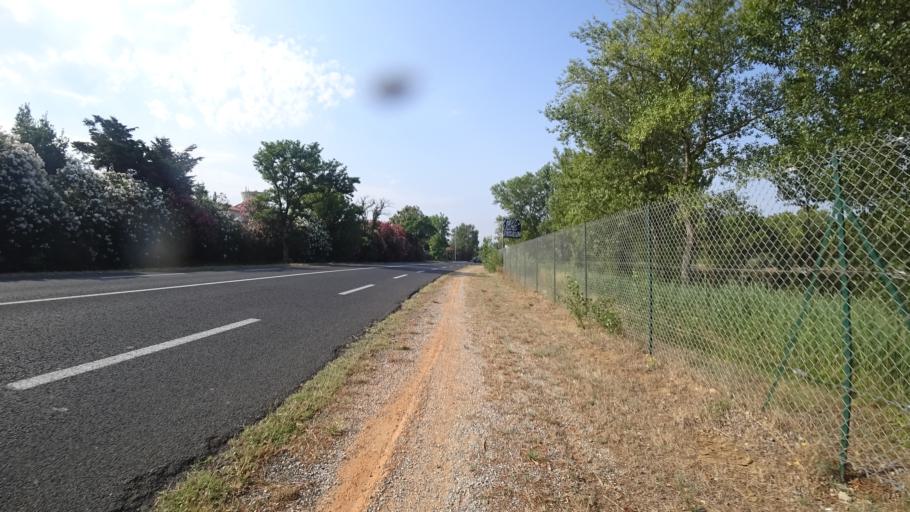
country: FR
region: Languedoc-Roussillon
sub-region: Departement des Pyrenees-Orientales
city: Canet-en-Roussillon
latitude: 42.6864
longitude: 3.0292
